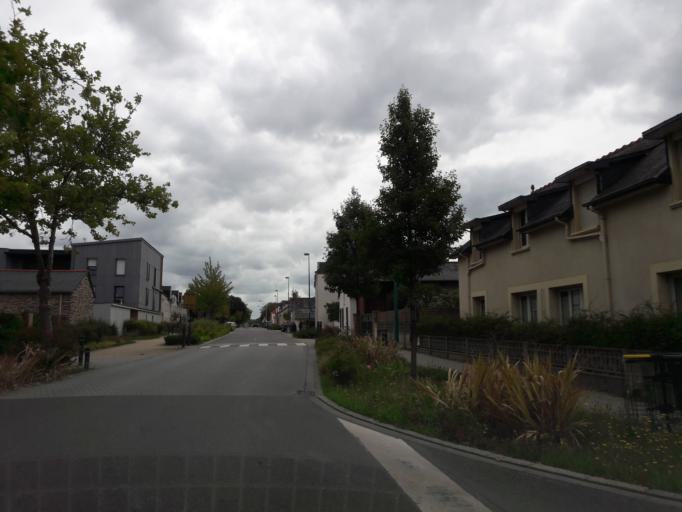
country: FR
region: Brittany
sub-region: Departement d'Ille-et-Vilaine
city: Chartres-de-Bretagne
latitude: 48.0153
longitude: -1.7037
